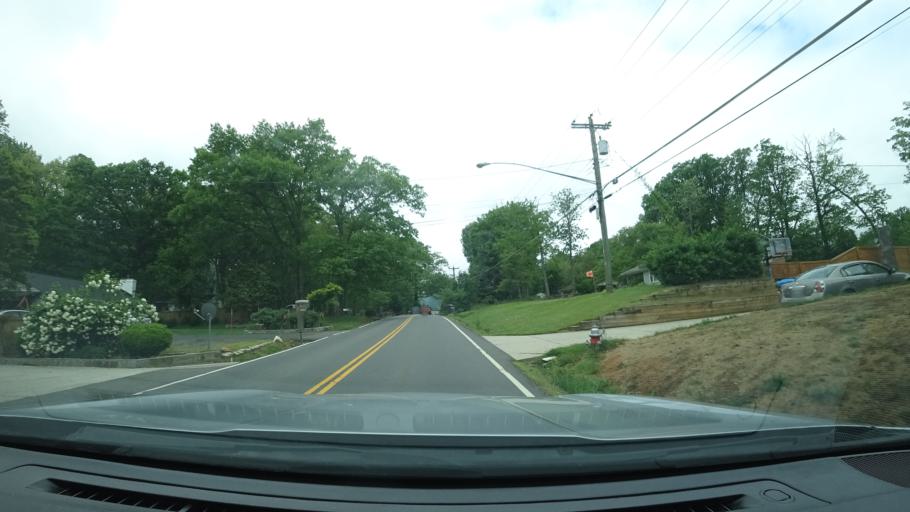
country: US
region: Virginia
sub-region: Fairfax County
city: Greenbriar
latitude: 38.8789
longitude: -77.3649
